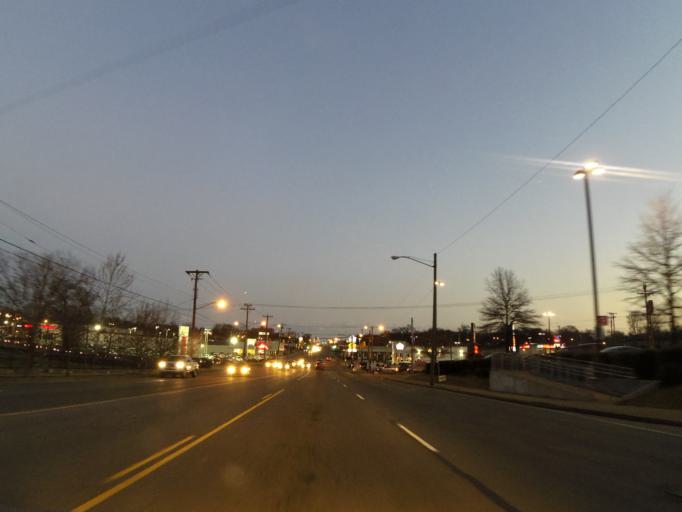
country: US
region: Tennessee
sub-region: Davidson County
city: Oak Hill
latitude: 36.1119
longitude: -86.7458
